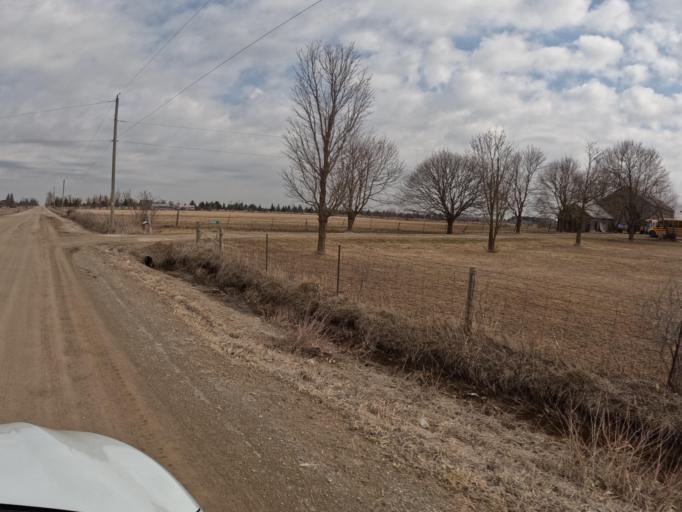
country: CA
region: Ontario
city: Orangeville
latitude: 43.9020
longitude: -80.2135
